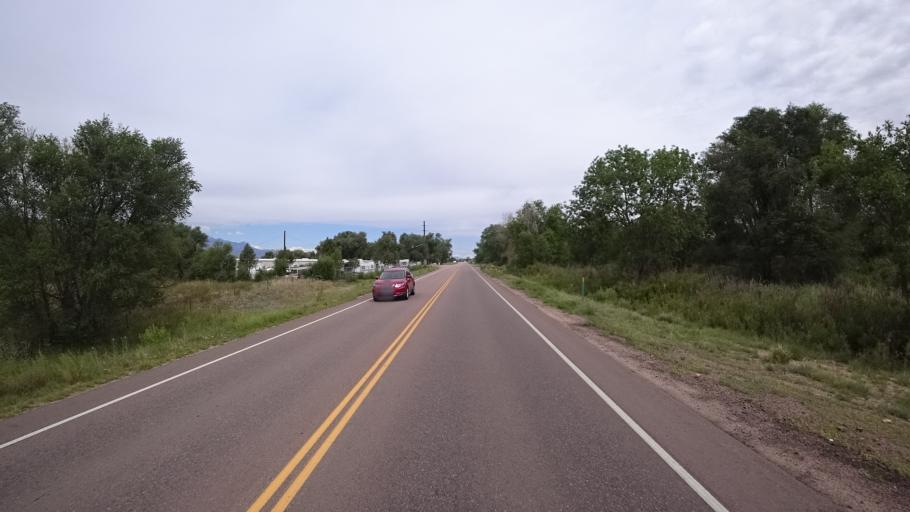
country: US
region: Colorado
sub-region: El Paso County
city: Fountain
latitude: 38.7037
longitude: -104.7093
